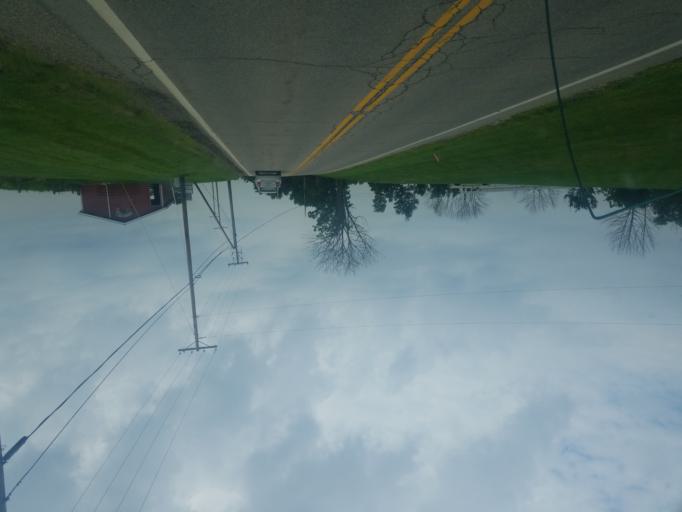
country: US
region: Ohio
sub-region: Carroll County
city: Carrollton
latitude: 40.6067
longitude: -81.0686
